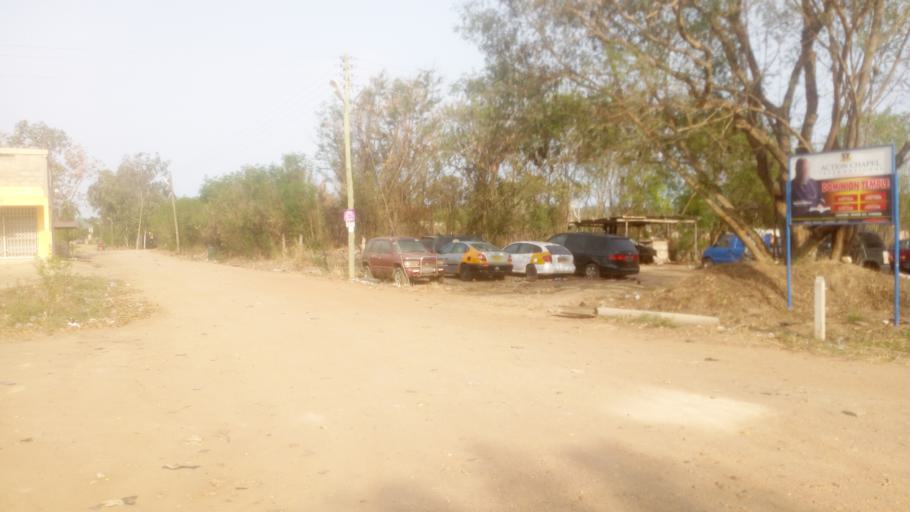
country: GH
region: Central
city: Winneba
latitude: 5.3783
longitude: -0.6407
